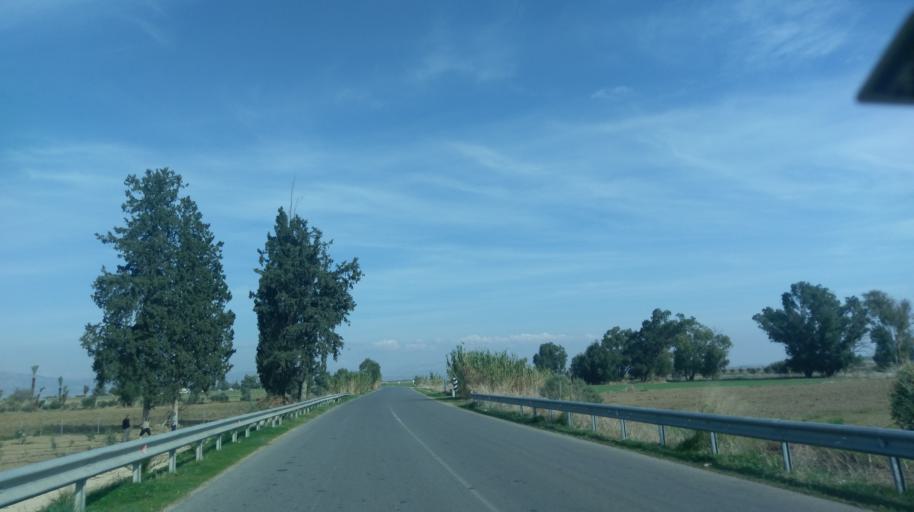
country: CY
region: Larnaka
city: Troulloi
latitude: 35.1543
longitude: 33.6377
